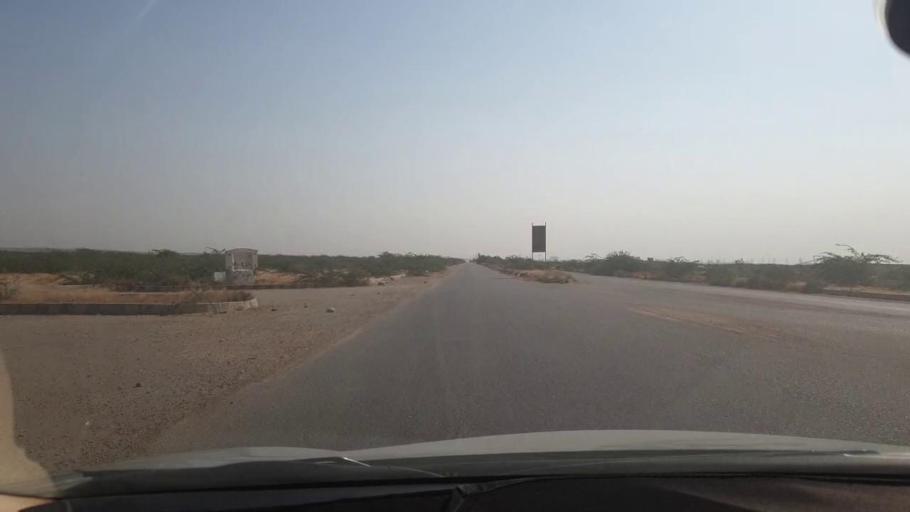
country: PK
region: Sindh
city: Malir Cantonment
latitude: 25.0723
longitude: 67.1386
